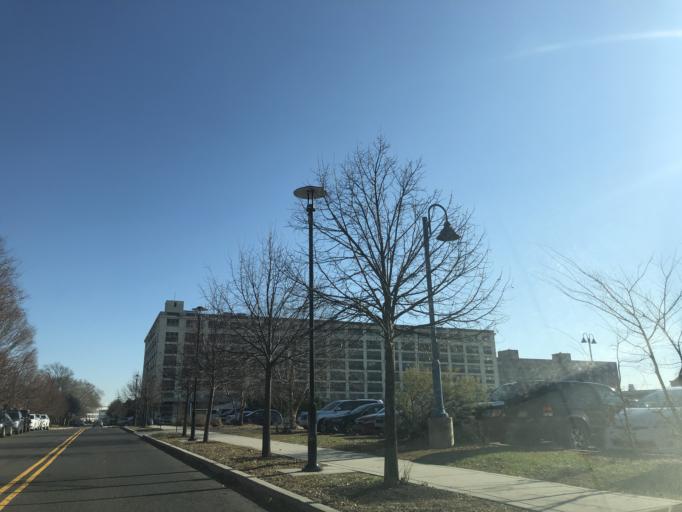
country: US
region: New Jersey
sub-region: Gloucester County
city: National Park
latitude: 39.8914
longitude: -75.1756
